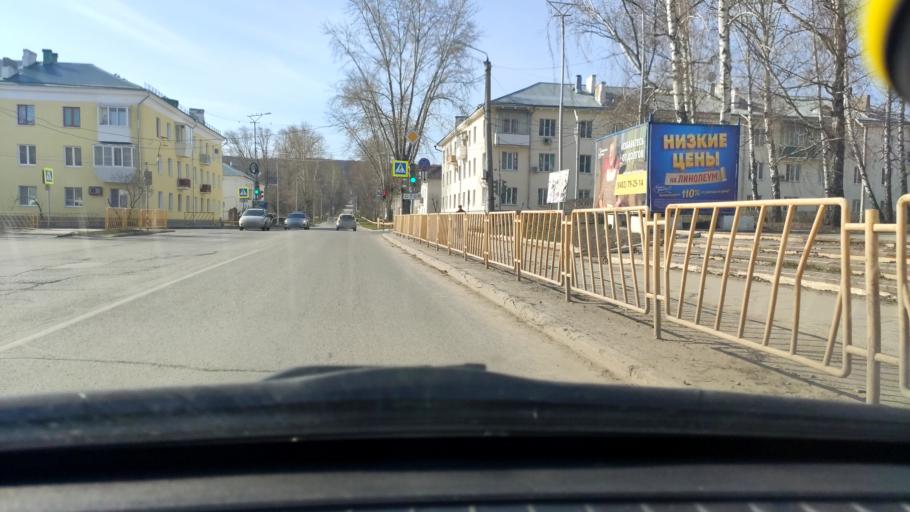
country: RU
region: Samara
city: Zhigulevsk
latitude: 53.4018
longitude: 49.4977
